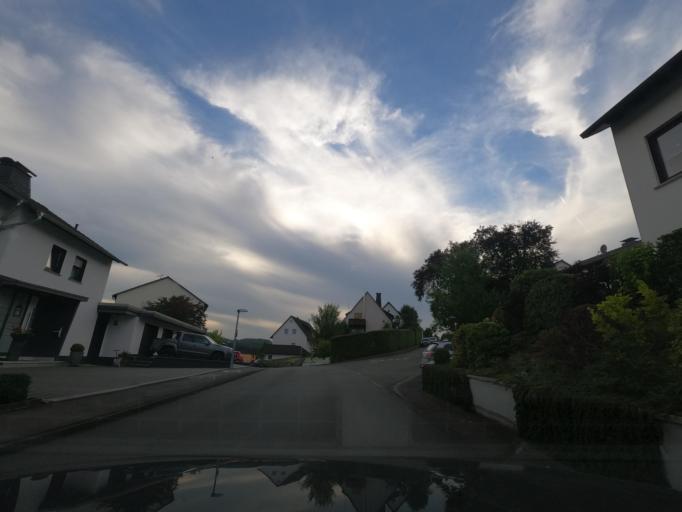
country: DE
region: North Rhine-Westphalia
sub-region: Regierungsbezirk Arnsberg
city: Herscheid
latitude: 51.1944
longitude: 7.7951
